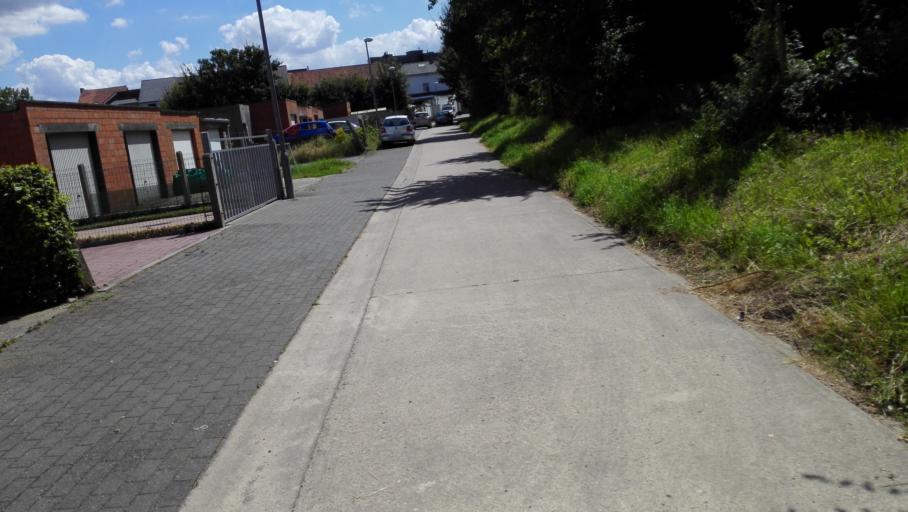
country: BE
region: Flanders
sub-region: Provincie Vlaams-Brabant
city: Tienen
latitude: 50.8023
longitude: 4.9265
